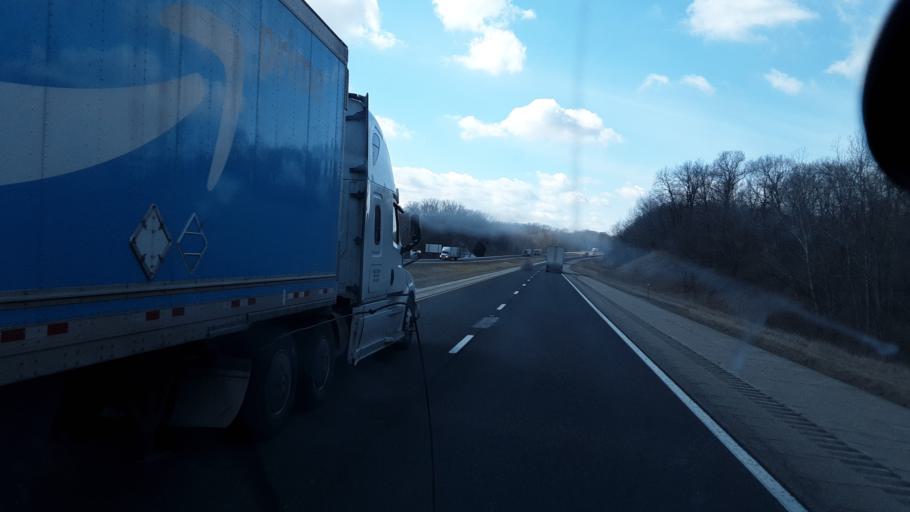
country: US
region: Illinois
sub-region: Clark County
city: Marshall
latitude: 39.4091
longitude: -87.7282
